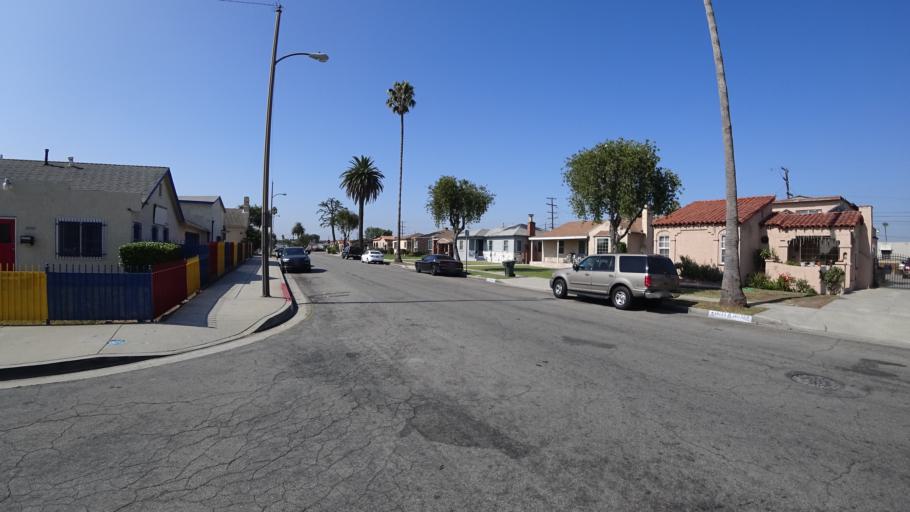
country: US
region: California
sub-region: Los Angeles County
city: Westmont
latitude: 33.9441
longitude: -118.3046
